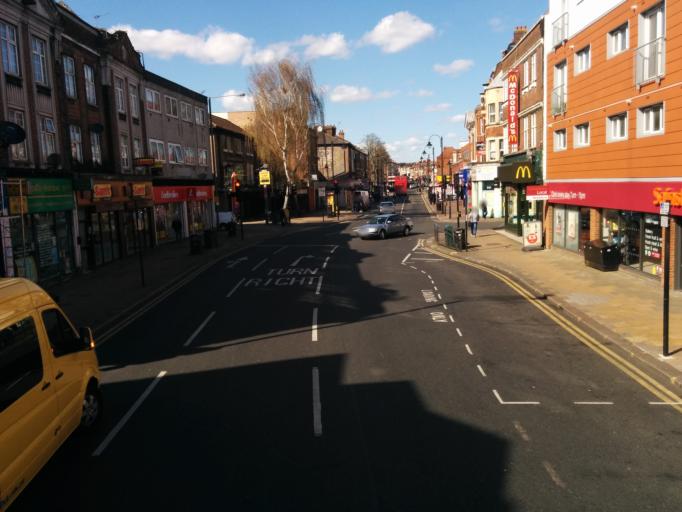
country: GB
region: England
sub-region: Greater London
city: Greenhill
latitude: 51.5932
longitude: -0.3350
